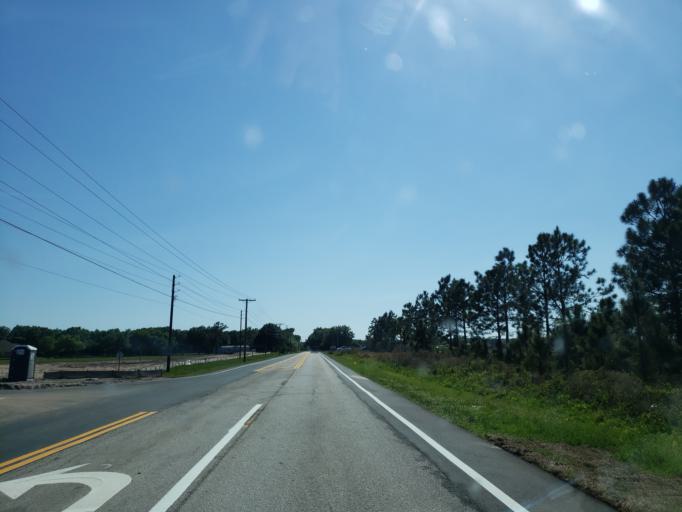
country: US
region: Florida
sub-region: Hillsborough County
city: Boyette
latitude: 27.8107
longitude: -82.2346
